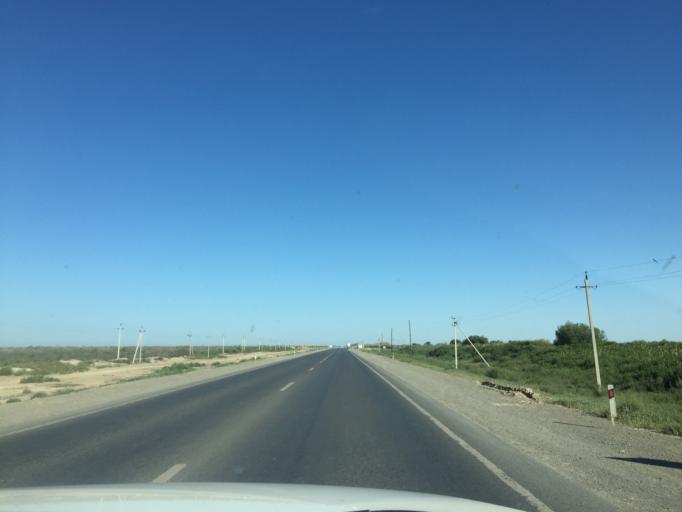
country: KZ
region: Qyzylorda
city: Kyzyl-Orda
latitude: 44.7961
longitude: 65.4534
